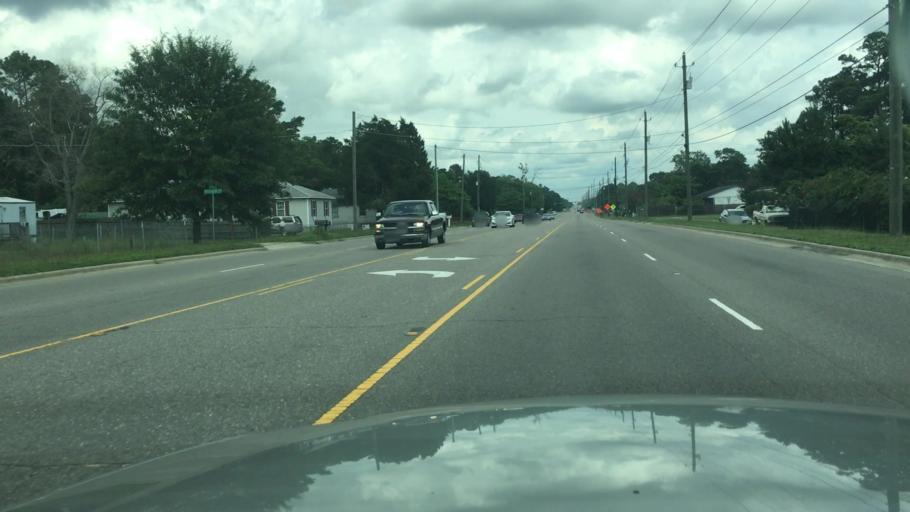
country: US
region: North Carolina
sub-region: Cumberland County
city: Hope Mills
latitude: 35.0117
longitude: -78.9459
